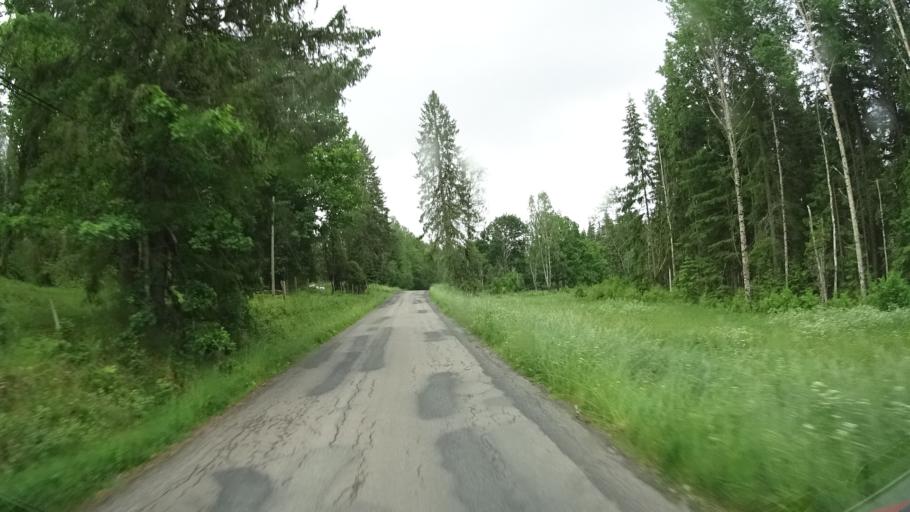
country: SE
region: Joenkoeping
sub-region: Eksjo Kommun
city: Mariannelund
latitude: 57.6867
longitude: 15.5676
